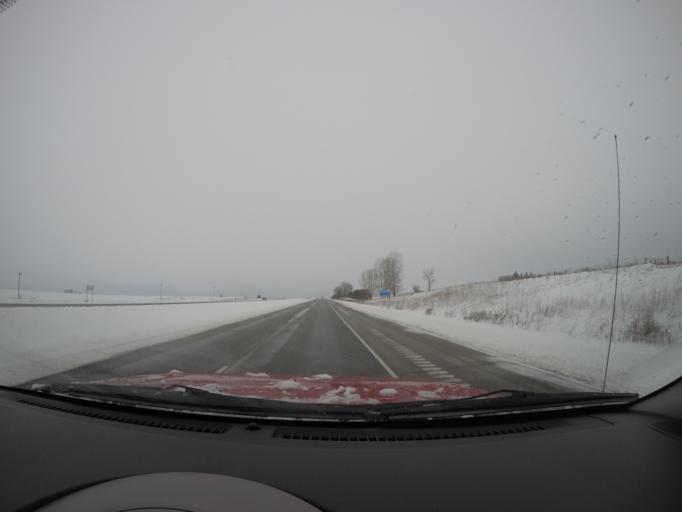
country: US
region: Minnesota
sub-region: Winona County
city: Goodview
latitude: 43.9438
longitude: -91.7240
